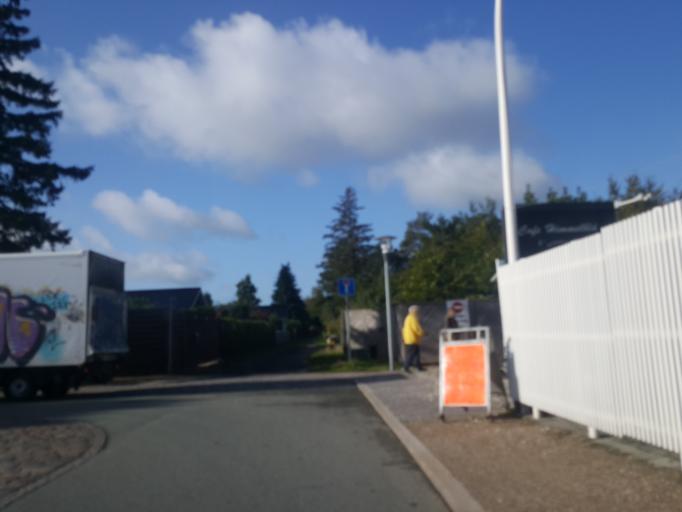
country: DK
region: Zealand
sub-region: Guldborgsund Kommune
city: Nykobing Falster
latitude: 54.6912
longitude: 11.9641
